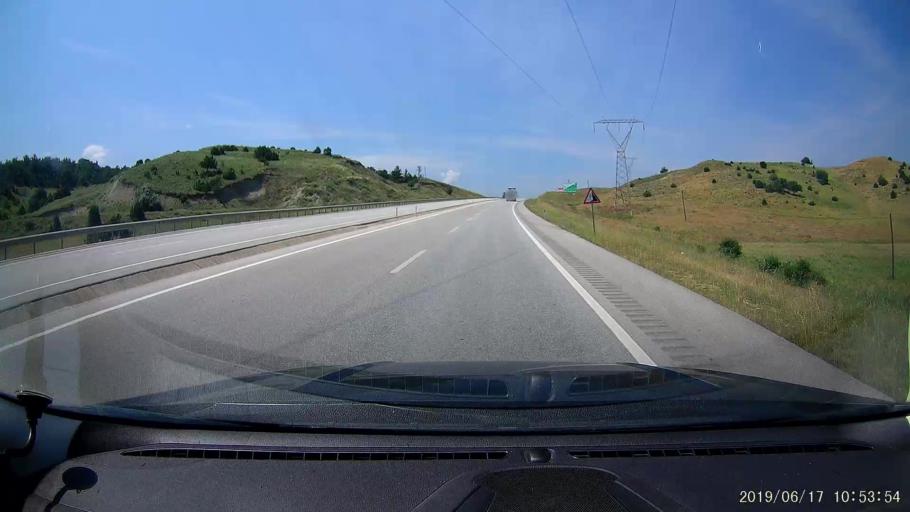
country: TR
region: Corum
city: Hacihamza
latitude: 41.0776
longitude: 34.3119
